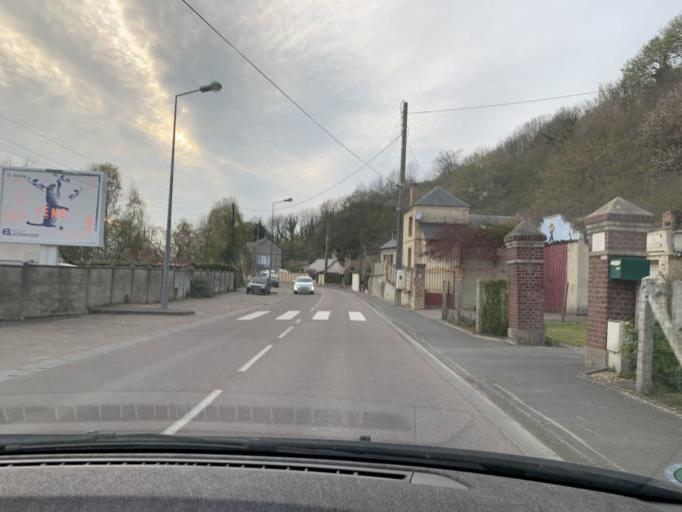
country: FR
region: Haute-Normandie
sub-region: Departement de la Seine-Maritime
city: Fecamp
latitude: 49.7538
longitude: 0.4067
